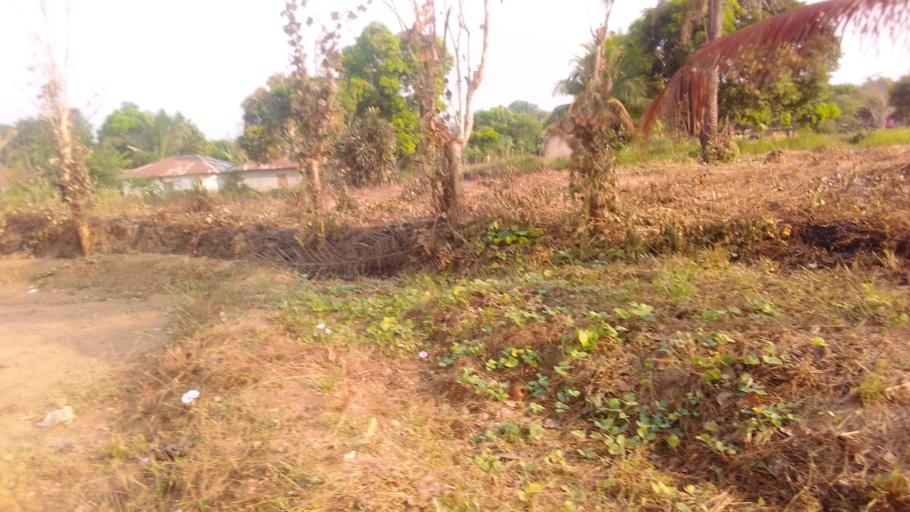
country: SL
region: Southern Province
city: Sumbuya
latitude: 7.6008
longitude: -12.1644
